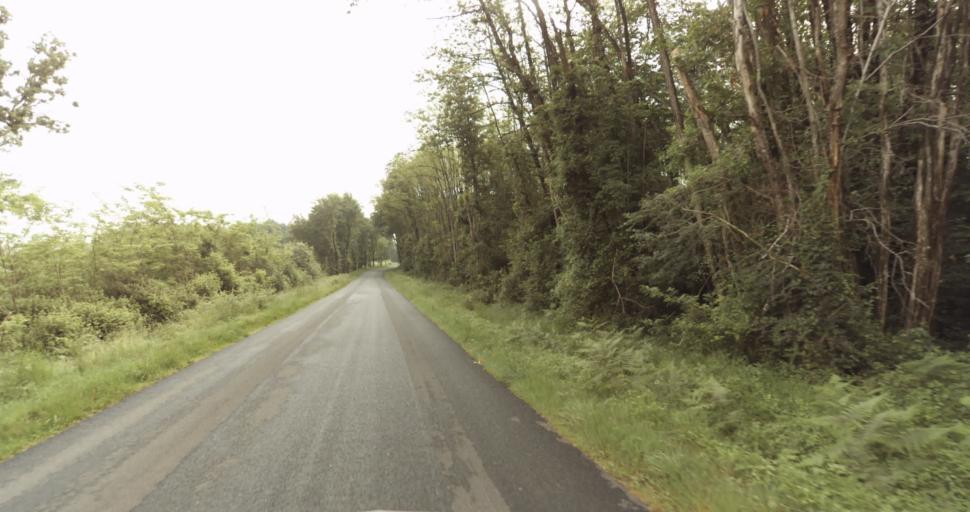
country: FR
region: Aquitaine
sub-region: Departement de la Dordogne
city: Lalinde
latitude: 44.9026
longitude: 0.7753
